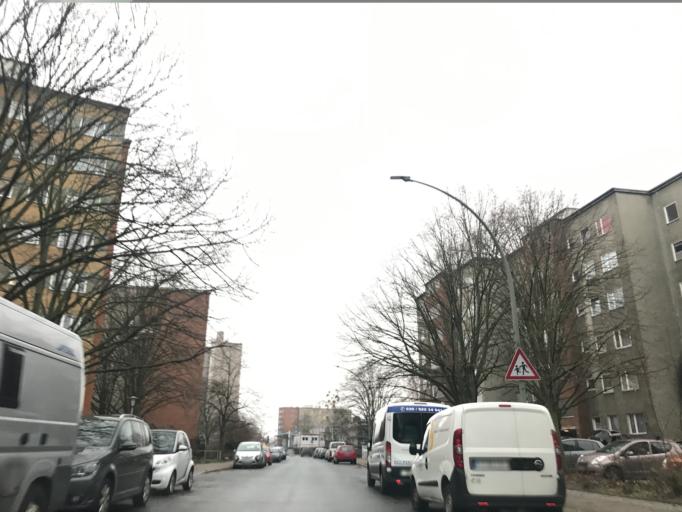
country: DE
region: Berlin
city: Falkenhagener Feld
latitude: 52.5528
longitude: 13.1792
